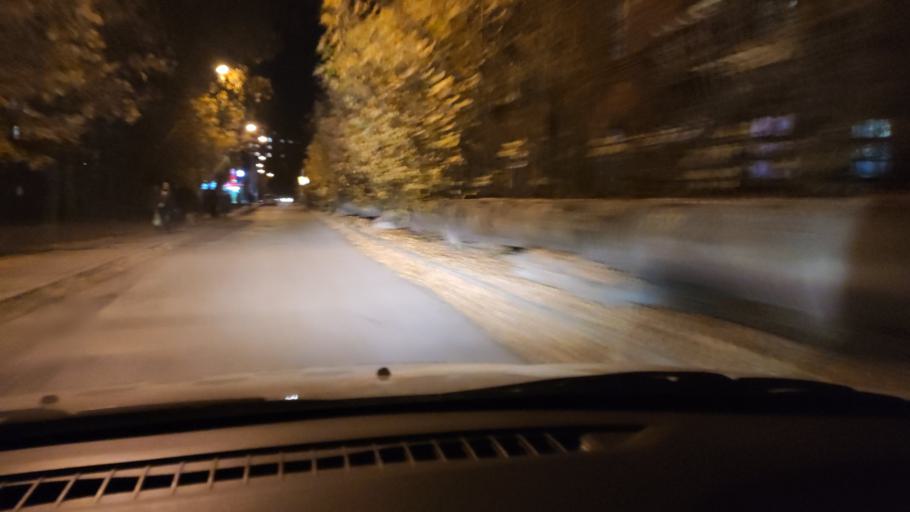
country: RU
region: Perm
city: Perm
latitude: 57.9742
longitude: 56.2734
